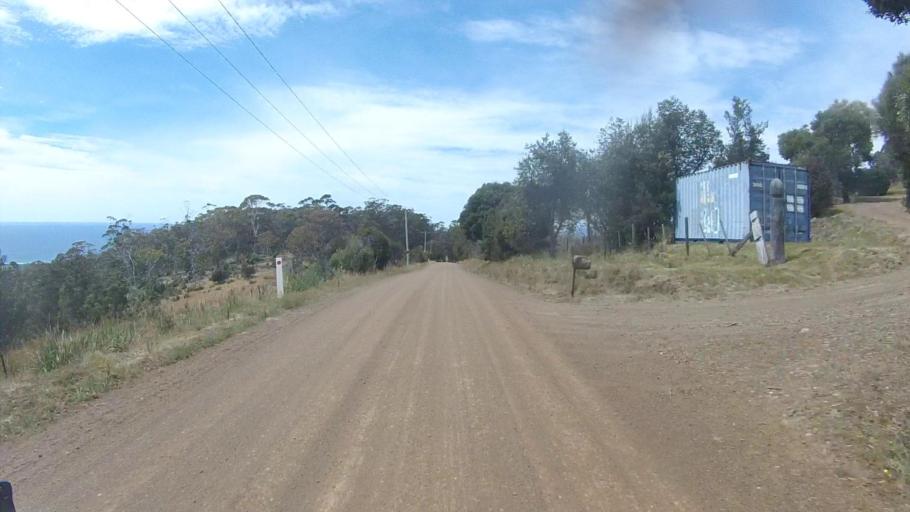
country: AU
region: Tasmania
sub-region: Sorell
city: Sorell
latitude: -42.7899
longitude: 147.8446
